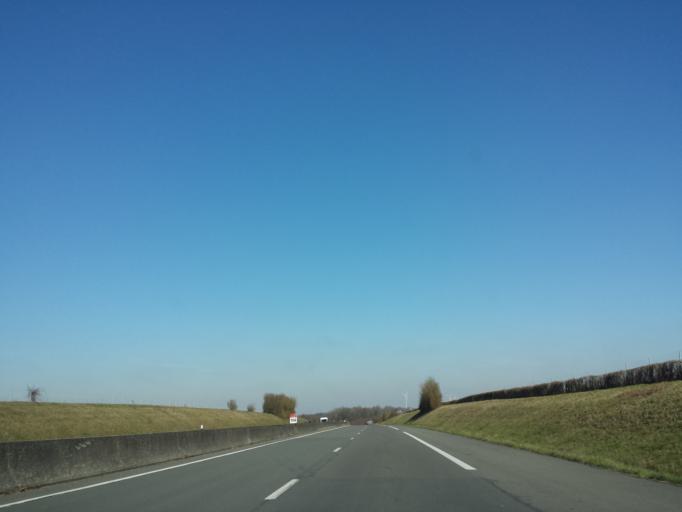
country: FR
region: Picardie
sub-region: Departement de la Somme
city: Conty
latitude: 49.7182
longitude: 2.2404
